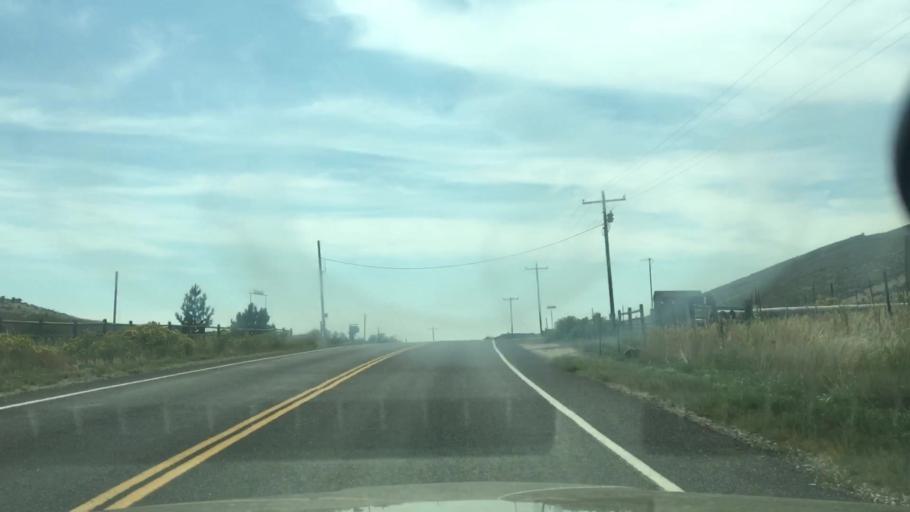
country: US
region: Colorado
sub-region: Larimer County
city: Campion
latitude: 40.3646
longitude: -105.1883
